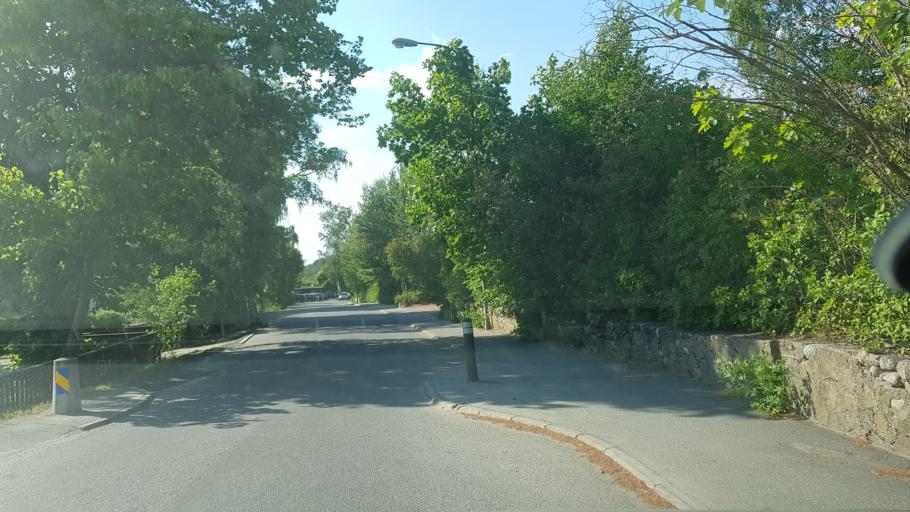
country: SE
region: Stockholm
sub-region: Sollentuna Kommun
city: Sollentuna
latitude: 59.4227
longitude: 17.9659
